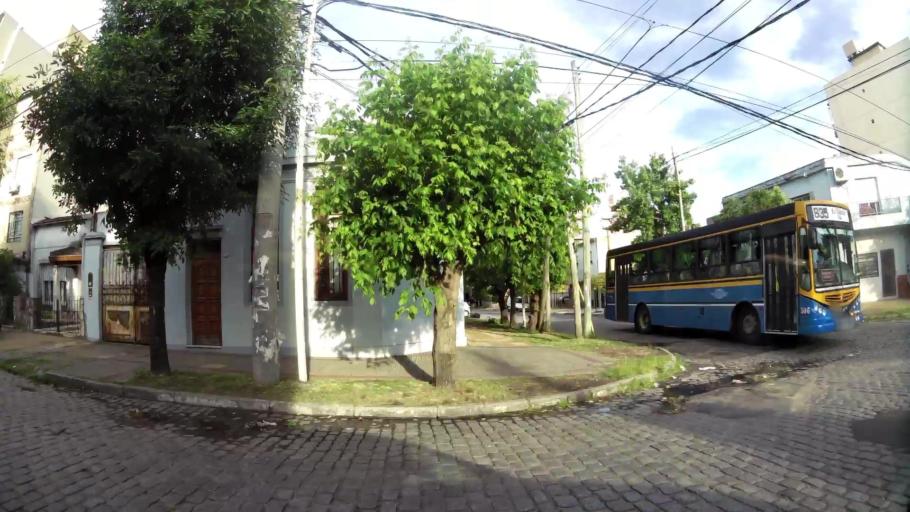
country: AR
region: Buenos Aires
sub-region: Partido de Moron
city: Moron
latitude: -34.6557
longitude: -58.6186
